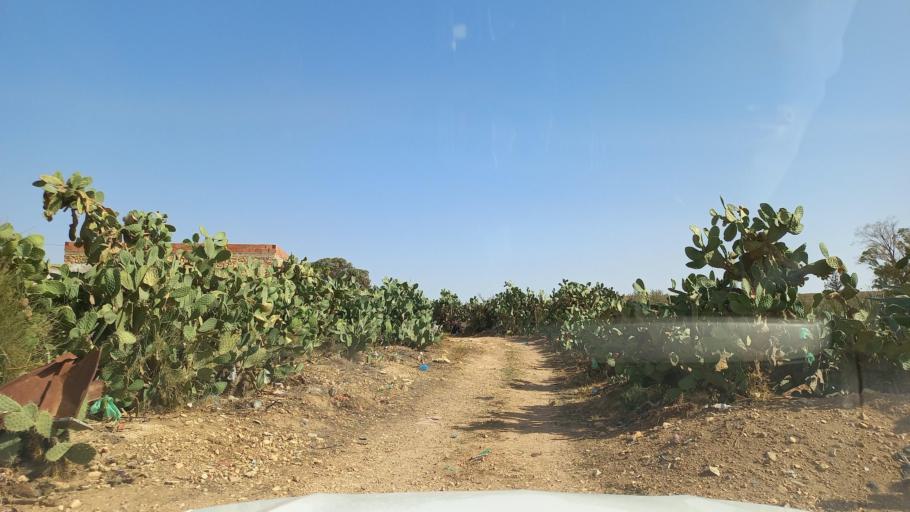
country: TN
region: Al Qasrayn
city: Kasserine
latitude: 35.2087
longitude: 8.9845
